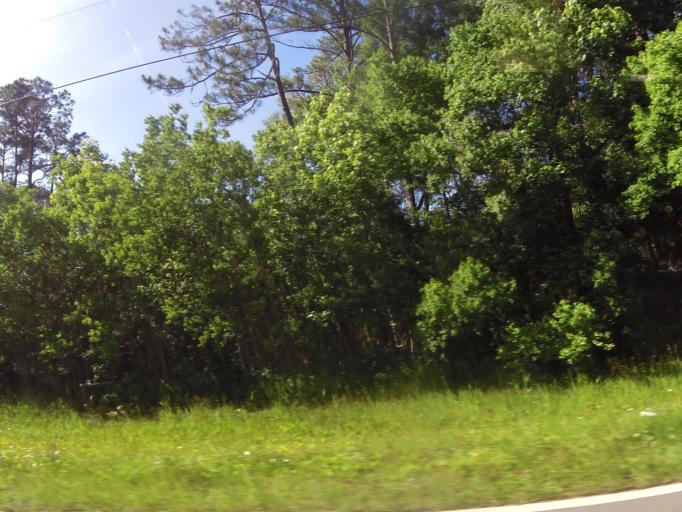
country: US
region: Florida
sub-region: Nassau County
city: Callahan
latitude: 30.5623
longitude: -81.8057
